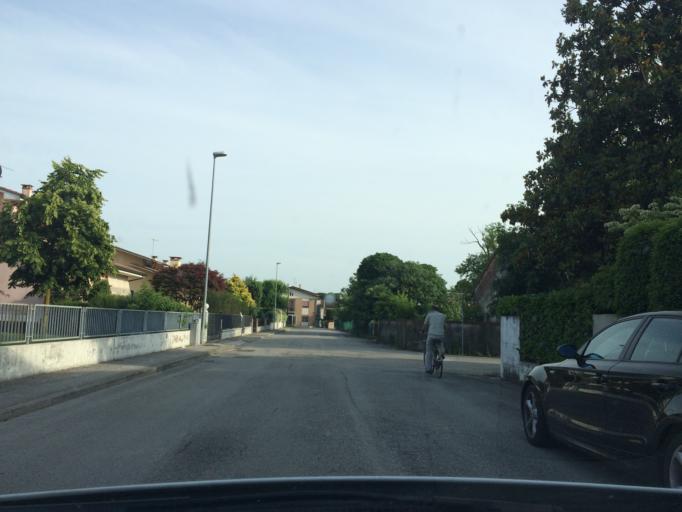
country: IT
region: Veneto
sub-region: Provincia di Padova
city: Cittadella
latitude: 45.6550
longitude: 11.7797
